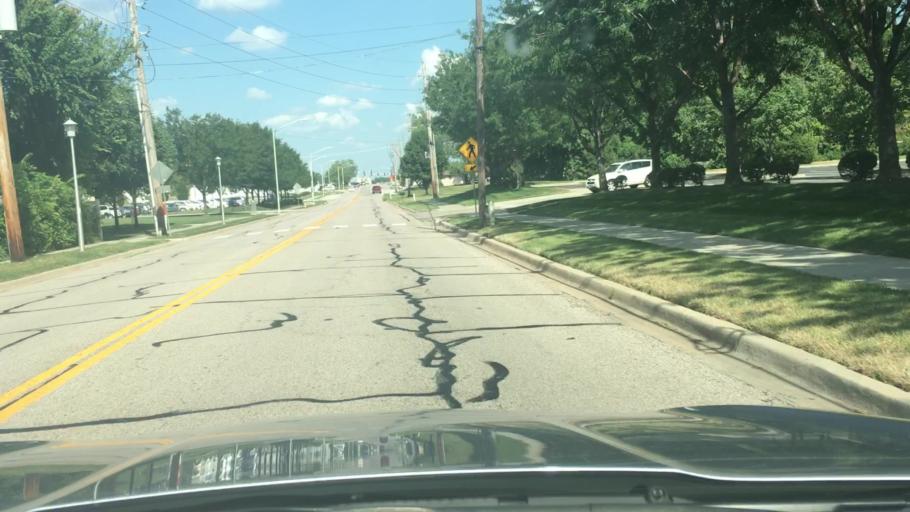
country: US
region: Missouri
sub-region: Jackson County
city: Lees Summit
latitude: 38.8962
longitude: -94.3810
